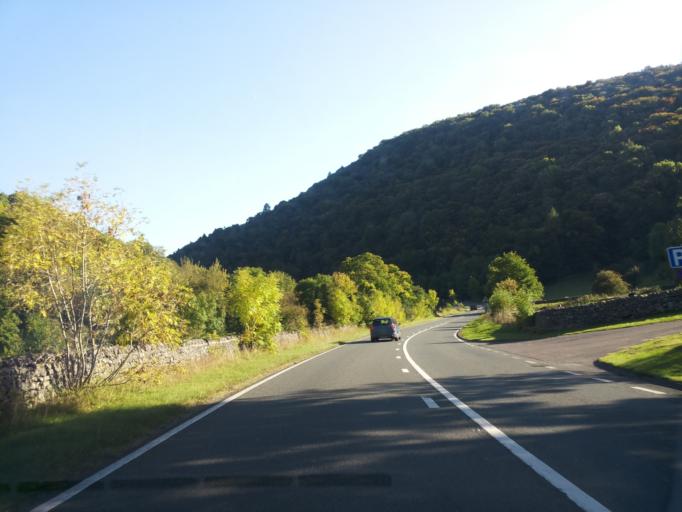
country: GB
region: England
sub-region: Derbyshire
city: Tideswell
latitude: 53.2321
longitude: -1.7453
